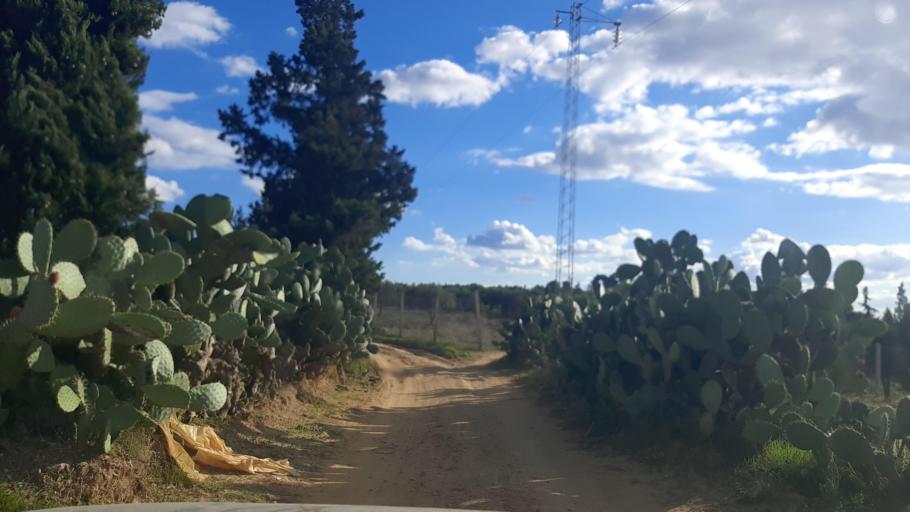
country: TN
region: Nabul
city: Bu `Urqub
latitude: 36.4520
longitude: 10.5001
